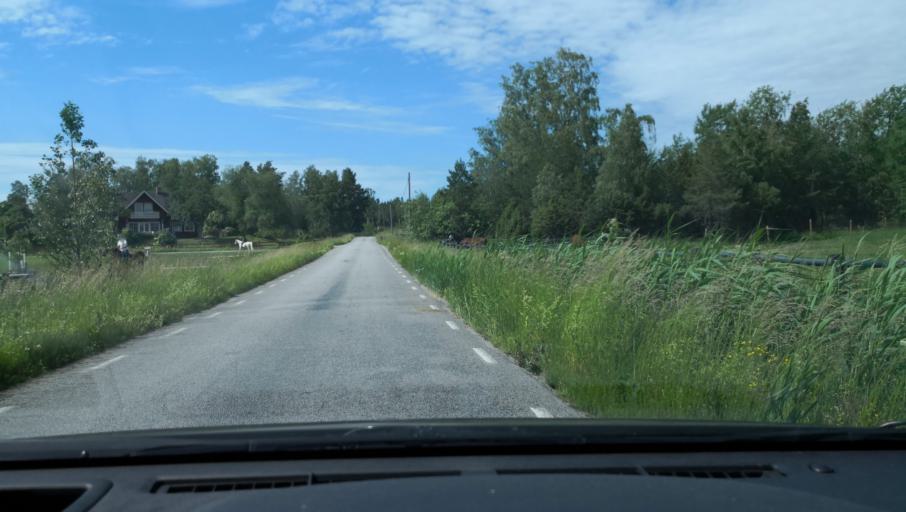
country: SE
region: Stockholm
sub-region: Sigtuna Kommun
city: Sigtuna
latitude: 59.6837
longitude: 17.6777
